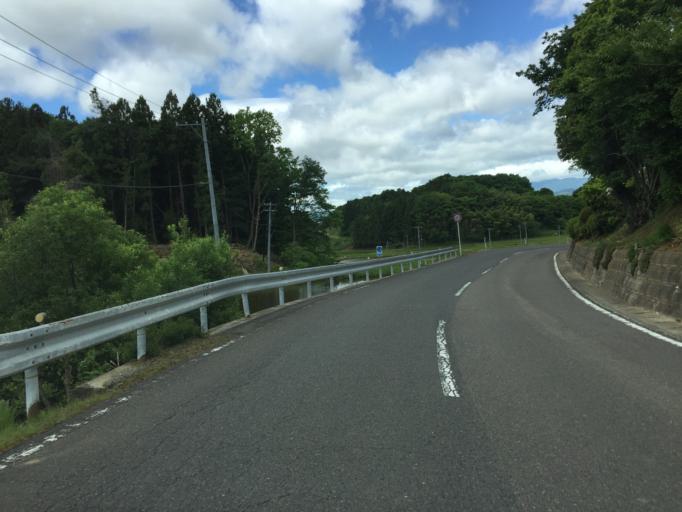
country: JP
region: Fukushima
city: Miharu
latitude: 37.4701
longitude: 140.4626
